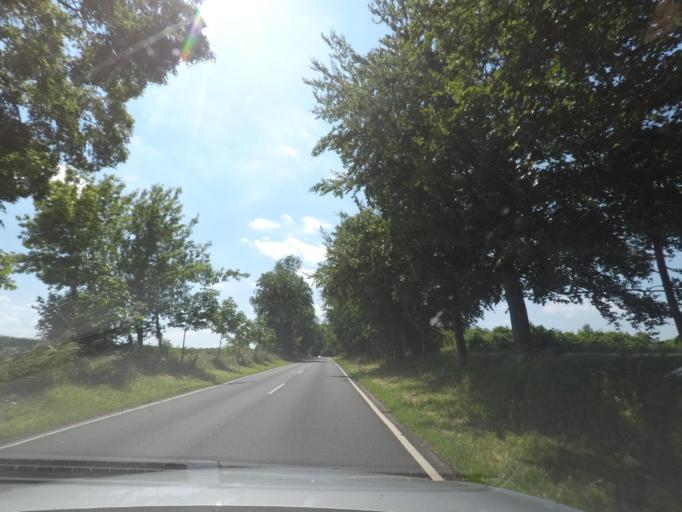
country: DE
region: Saxony-Anhalt
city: Haldensleben I
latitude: 52.2511
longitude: 11.4085
